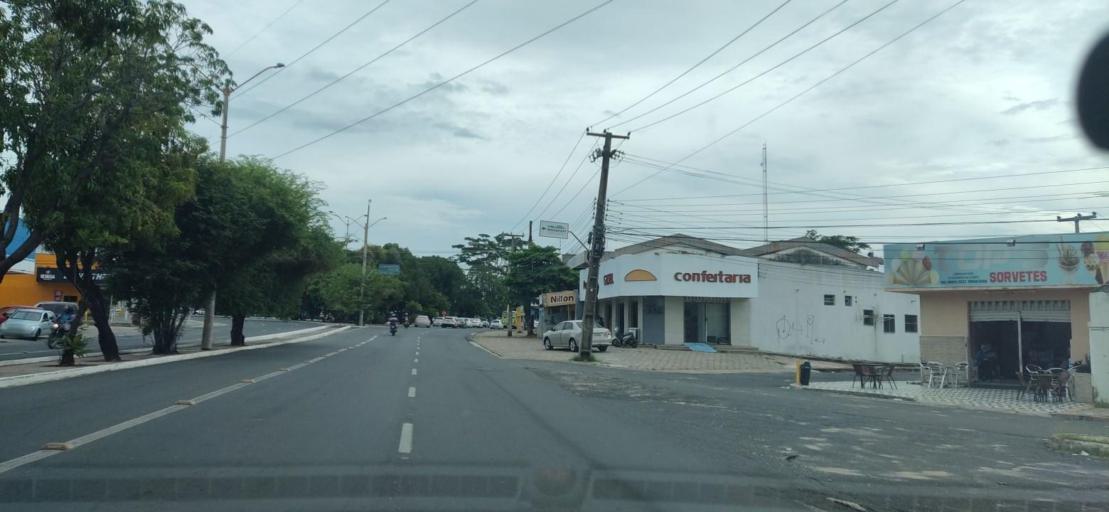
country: BR
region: Piaui
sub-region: Teresina
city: Teresina
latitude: -5.0794
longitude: -42.7746
